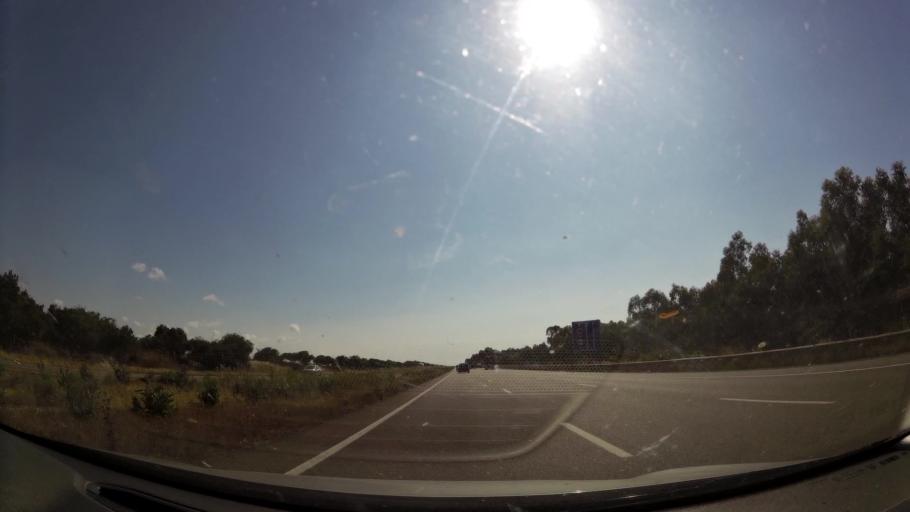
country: MA
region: Chaouia-Ouardigha
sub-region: Benslimane
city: Bouznika
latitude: 33.7950
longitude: -7.1874
